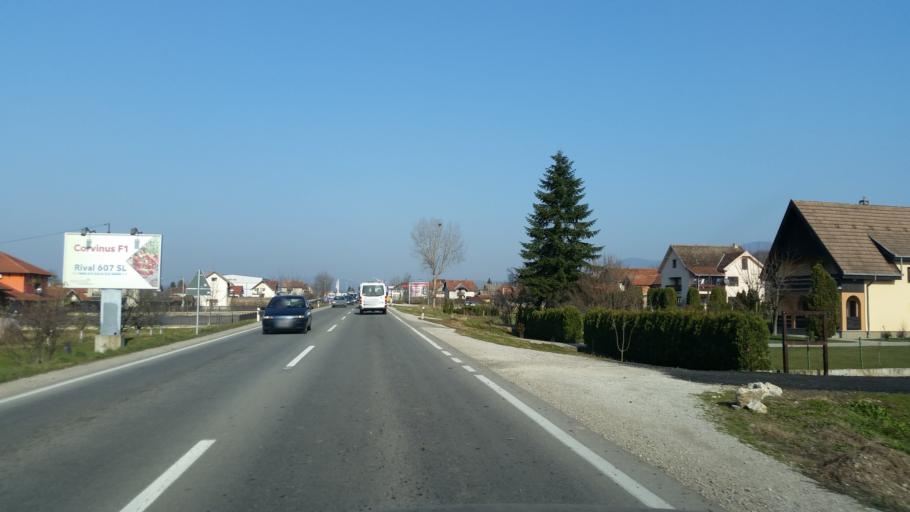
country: RS
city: Prislonica
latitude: 43.9215
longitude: 20.4088
